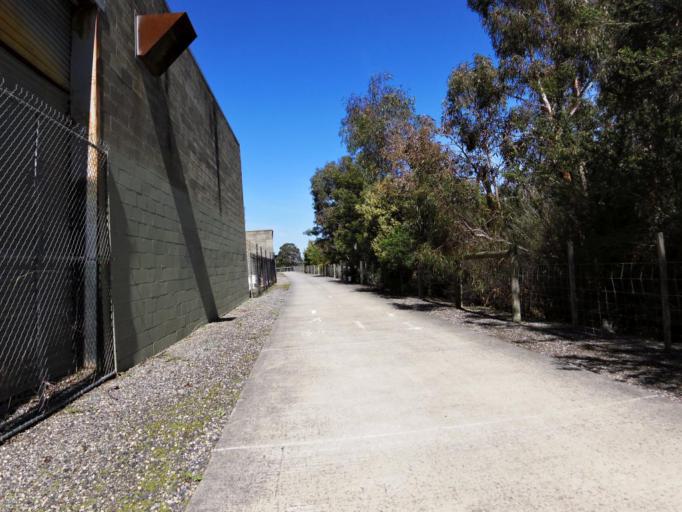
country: AU
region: Victoria
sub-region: Greater Dandenong
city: Dandenong
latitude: -37.9940
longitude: 145.1925
